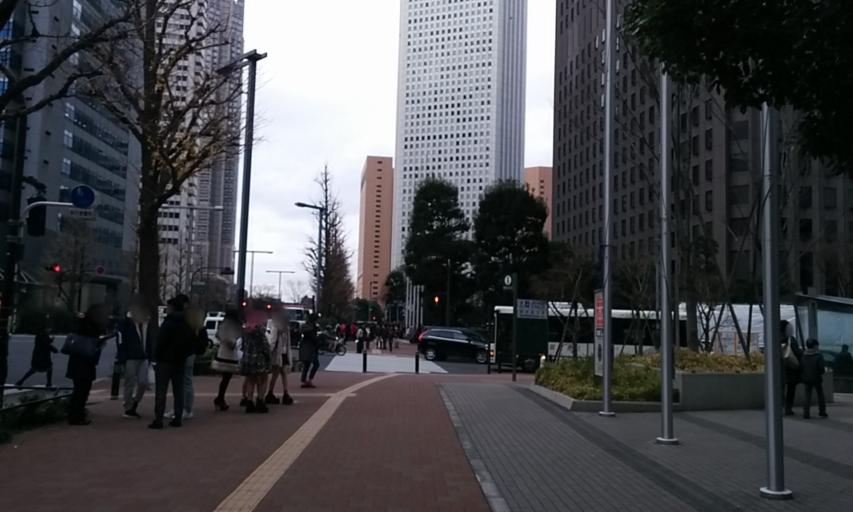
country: JP
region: Tokyo
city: Tokyo
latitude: 35.6912
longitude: 139.6967
